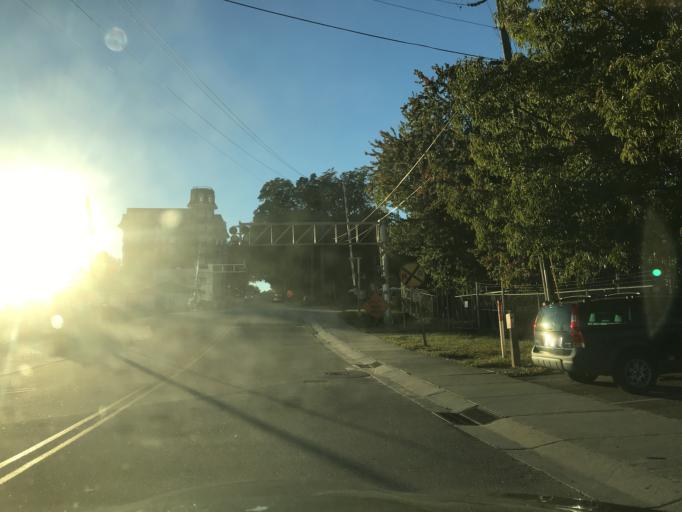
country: US
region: North Carolina
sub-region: Wake County
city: Raleigh
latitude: 35.7786
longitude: -78.6474
